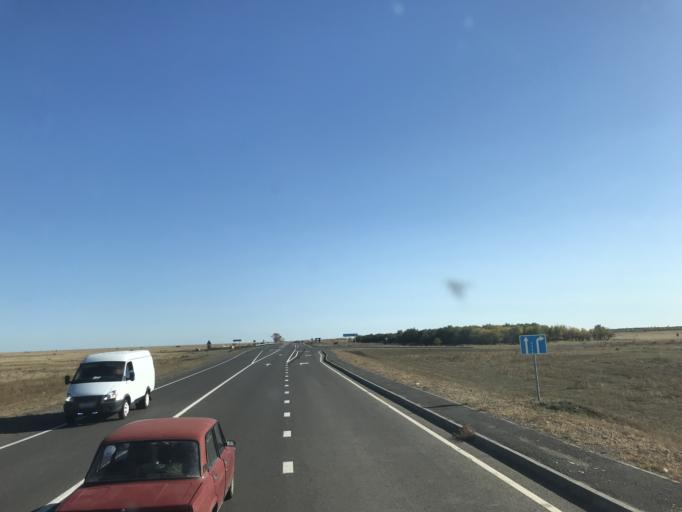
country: KZ
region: Pavlodar
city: Aksu
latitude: 52.0187
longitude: 77.2320
